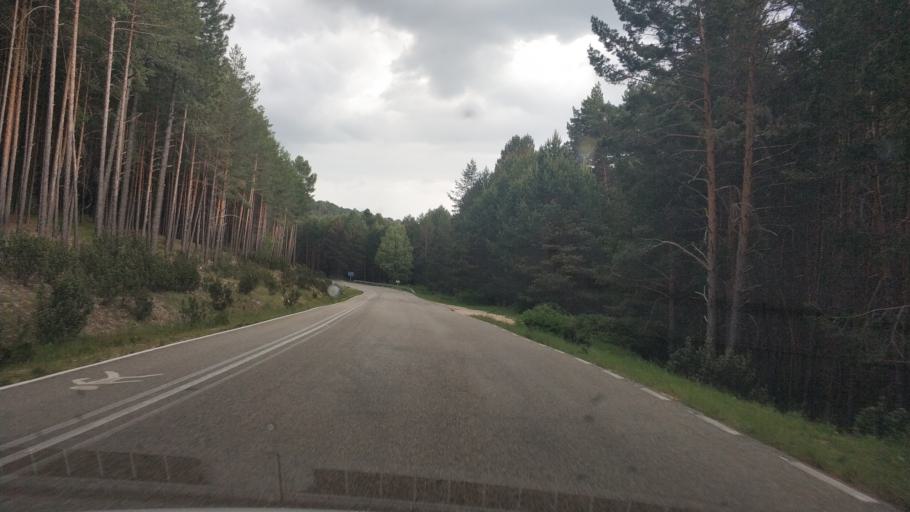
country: ES
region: Castille and Leon
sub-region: Provincia de Soria
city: San Leonardo de Yague
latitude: 41.8426
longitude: -3.0673
